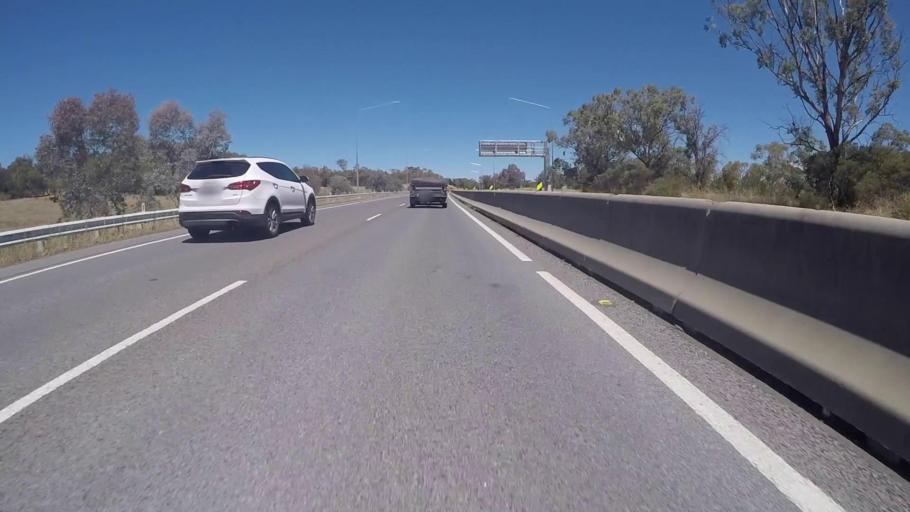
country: AU
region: Australian Capital Territory
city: Forrest
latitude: -35.3587
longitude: 149.0691
